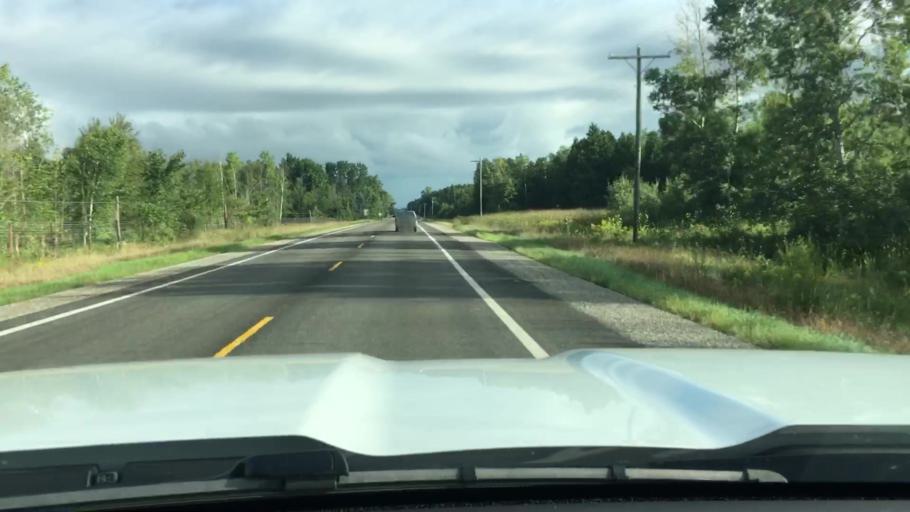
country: US
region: Michigan
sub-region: Tuscola County
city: Caro
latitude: 43.4174
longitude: -83.3843
